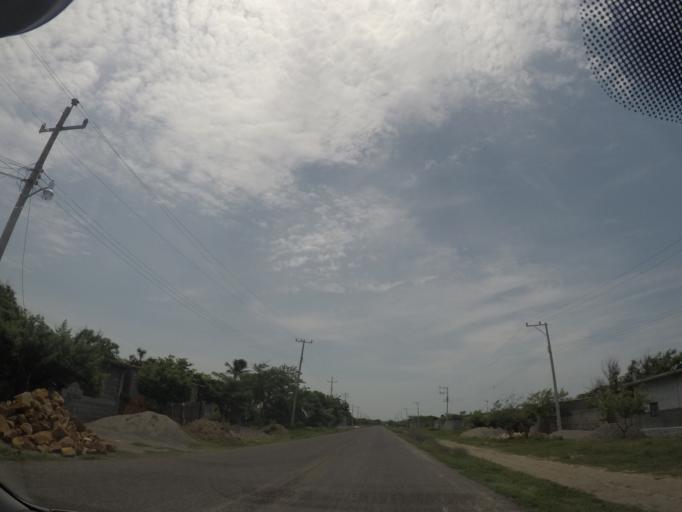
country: MX
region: Oaxaca
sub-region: San Mateo del Mar
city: Colonia Juarez
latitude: 16.2093
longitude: -95.0221
